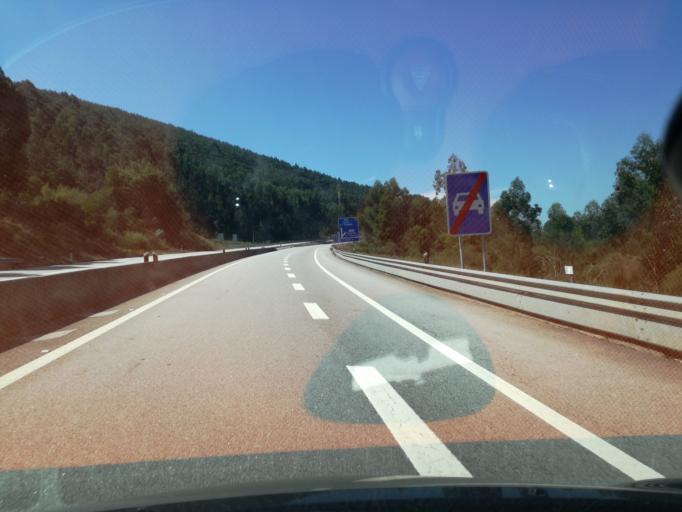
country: PT
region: Viana do Castelo
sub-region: Vila Nova de Cerveira
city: Vila Nova de Cerveira
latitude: 41.8877
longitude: -8.7760
